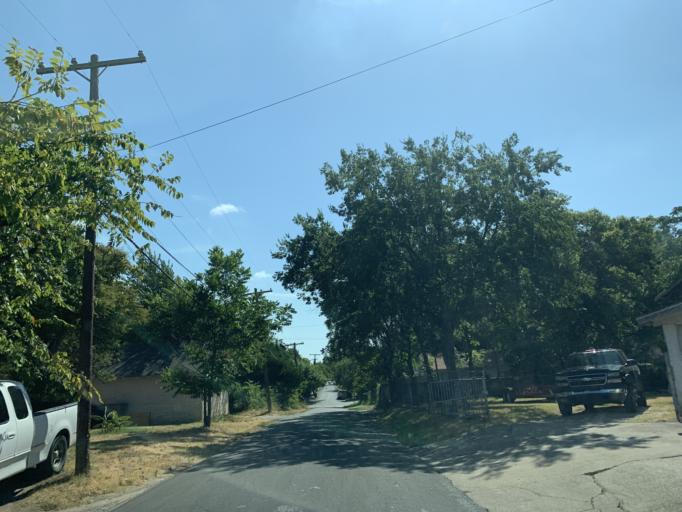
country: US
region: Texas
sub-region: Dallas County
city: Cockrell Hill
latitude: 32.7384
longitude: -96.8727
